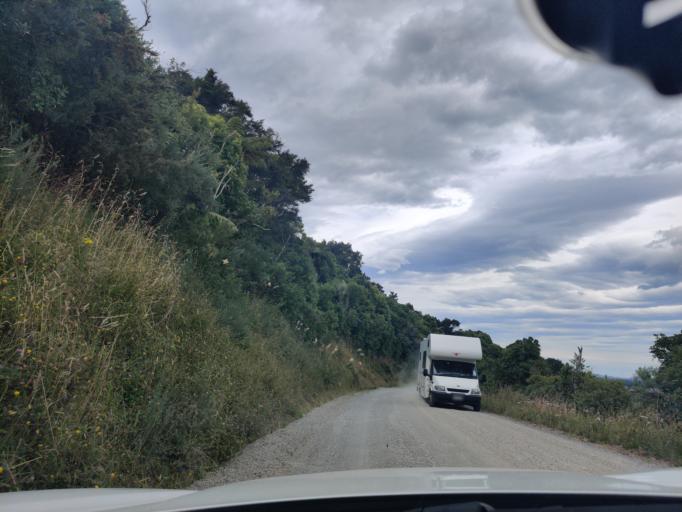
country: NZ
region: Wellington
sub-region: Masterton District
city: Masterton
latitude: -41.0381
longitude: 175.4155
